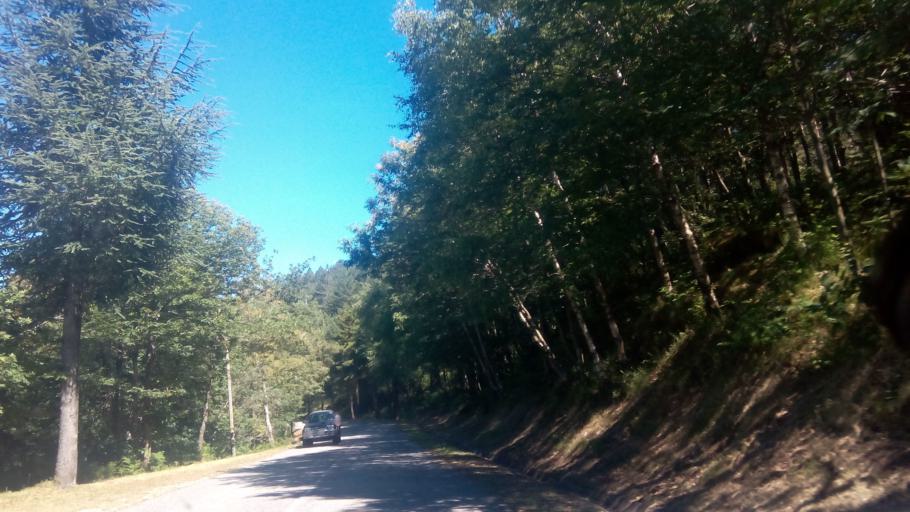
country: PT
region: Vila Real
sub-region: Mesao Frio
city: Mesao Frio
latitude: 41.2761
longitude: -7.9013
